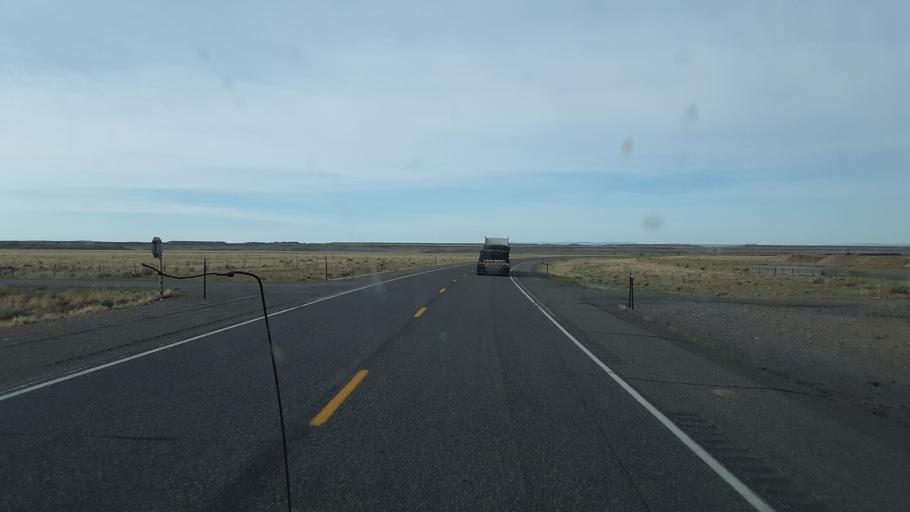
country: US
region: Wyoming
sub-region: Hot Springs County
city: Thermopolis
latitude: 43.3631
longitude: -108.1152
